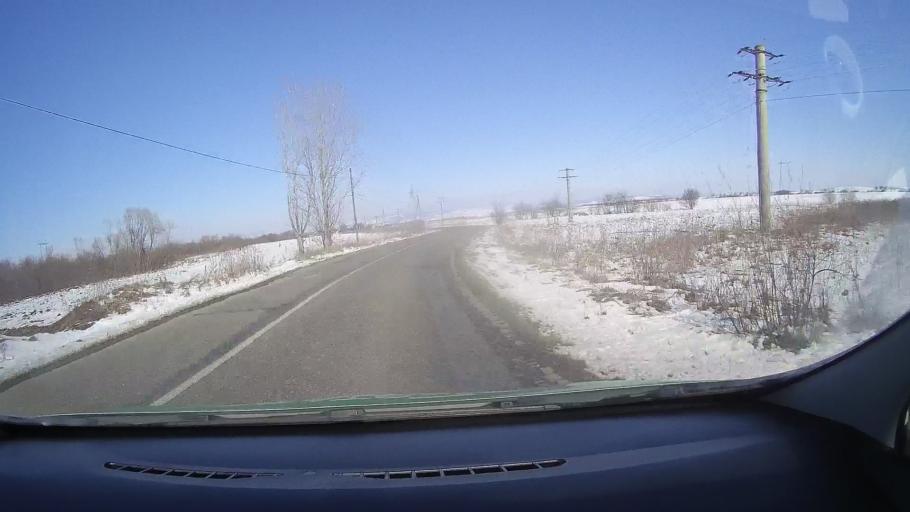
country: RO
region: Brasov
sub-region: Comuna Harseni
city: Harseni
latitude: 45.7723
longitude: 25.0012
